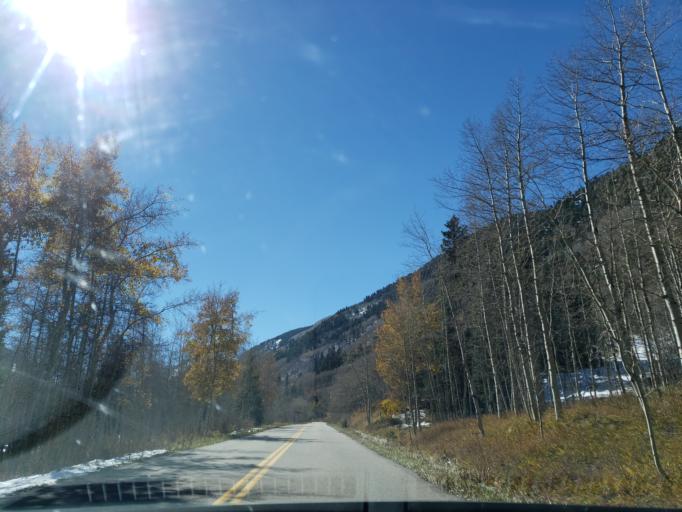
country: US
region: Colorado
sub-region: Pitkin County
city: Snowmass Village
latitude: 39.1434
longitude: -106.8952
